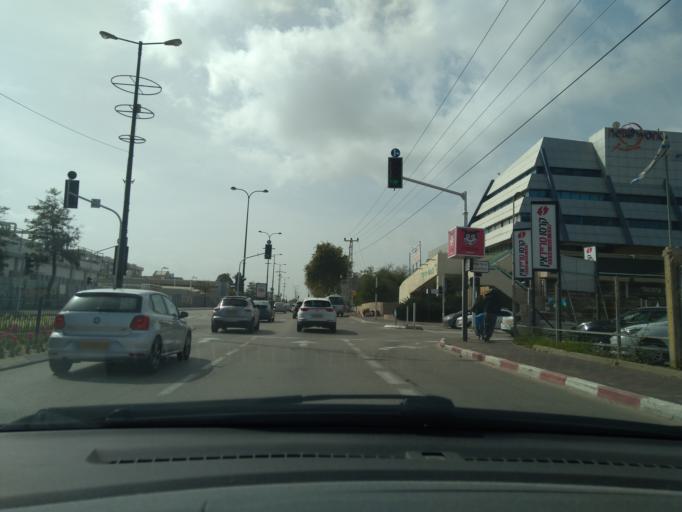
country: IL
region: Central District
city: Even Yehuda
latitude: 32.2854
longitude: 34.8624
